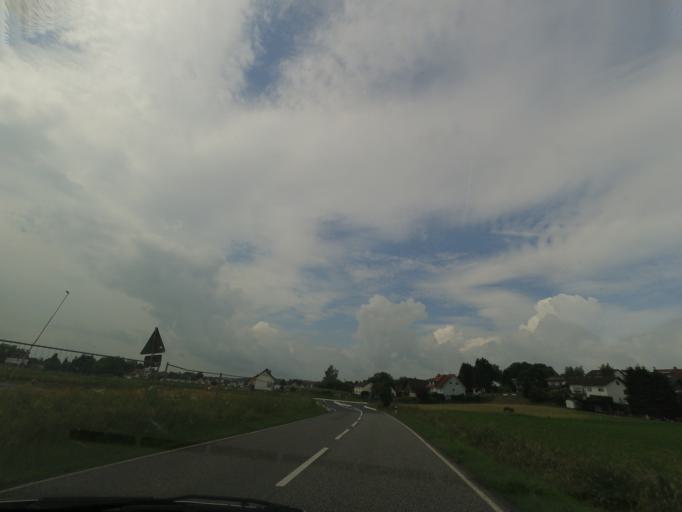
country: DE
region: Hesse
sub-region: Regierungsbezirk Giessen
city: Fronhausen
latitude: 50.7409
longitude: 8.7069
